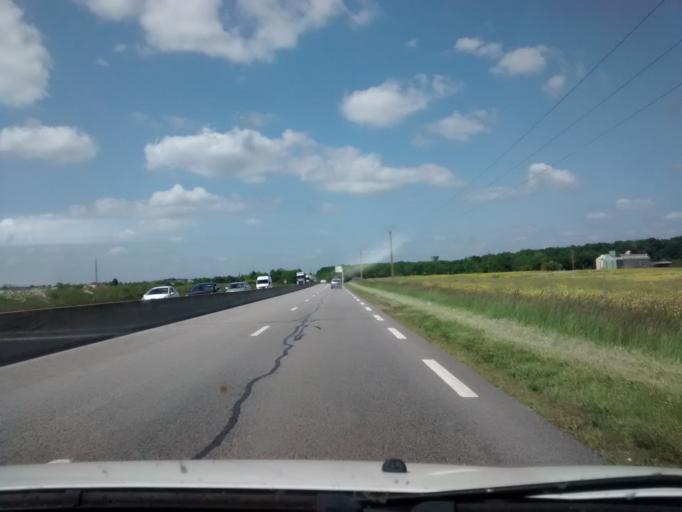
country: FR
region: Ile-de-France
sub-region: Departement des Yvelines
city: Rambouillet
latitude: 48.6154
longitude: 1.8314
